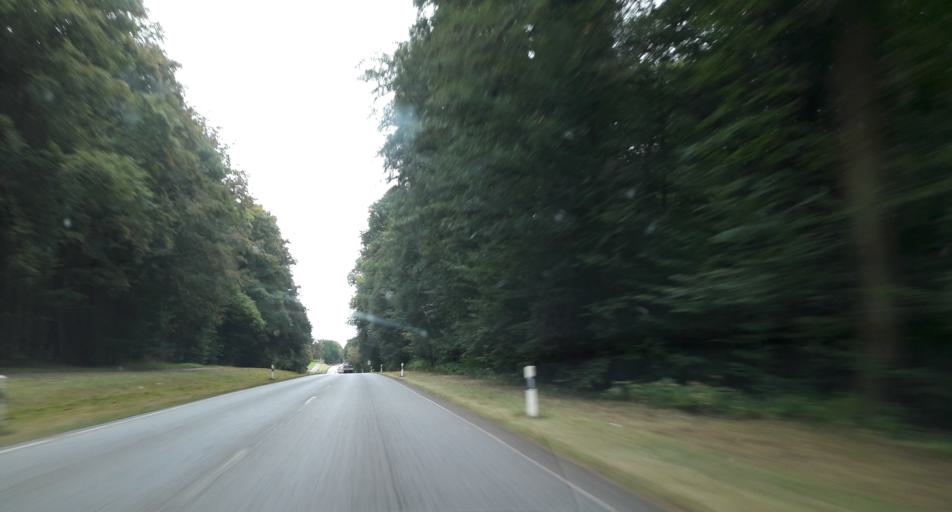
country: DE
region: Baden-Wuerttemberg
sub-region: Regierungsbezirk Stuttgart
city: Bad Rappenau
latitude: 49.2205
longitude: 9.1237
